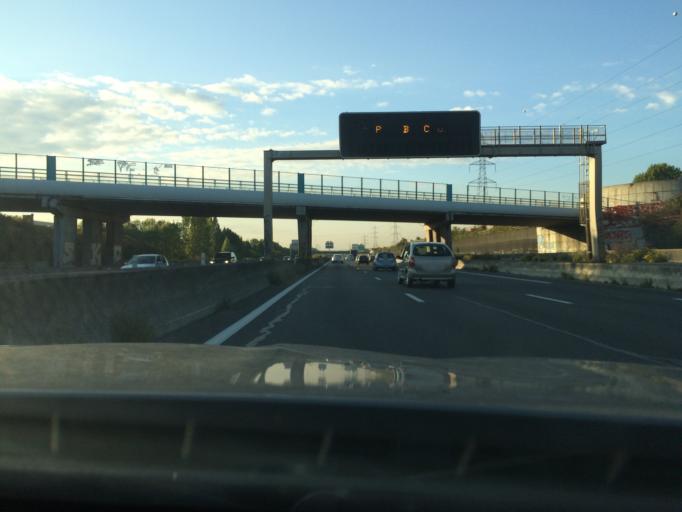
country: FR
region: Ile-de-France
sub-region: Departement de l'Essonne
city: Courcouronnes
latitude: 48.6262
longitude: 2.4162
